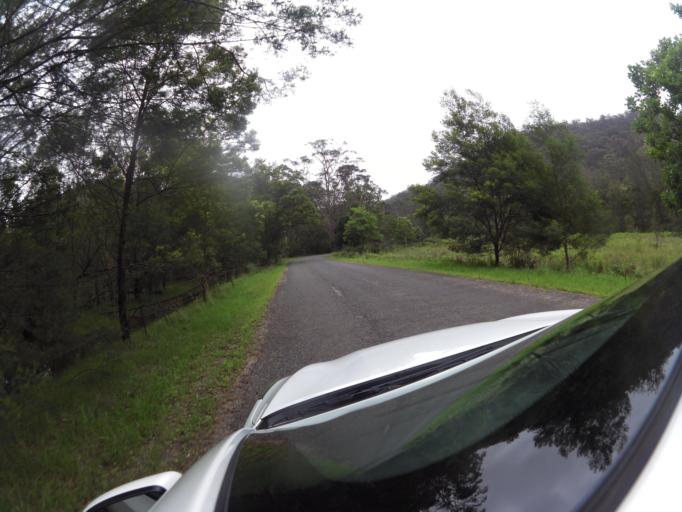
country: AU
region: New South Wales
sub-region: Hawkesbury
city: Pitt Town
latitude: -33.4330
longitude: 150.9461
